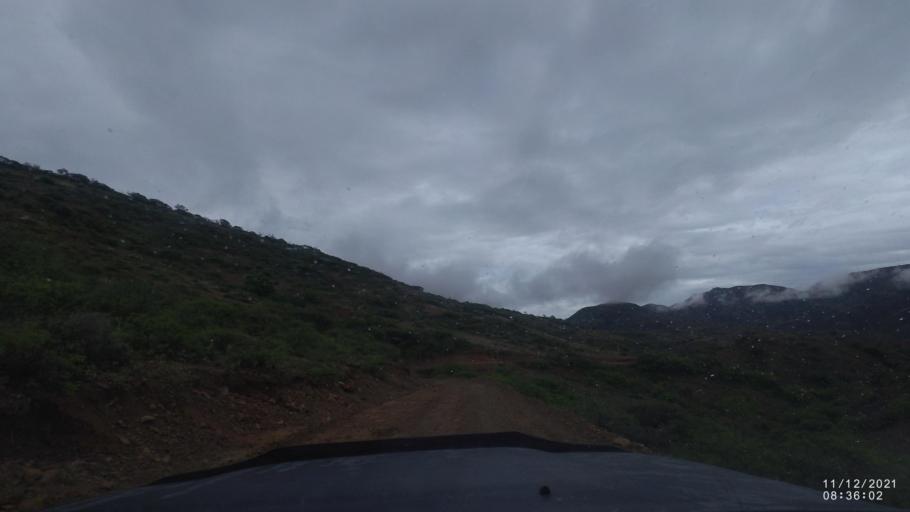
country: BO
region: Cochabamba
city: Tarata
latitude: -17.9289
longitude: -65.9363
